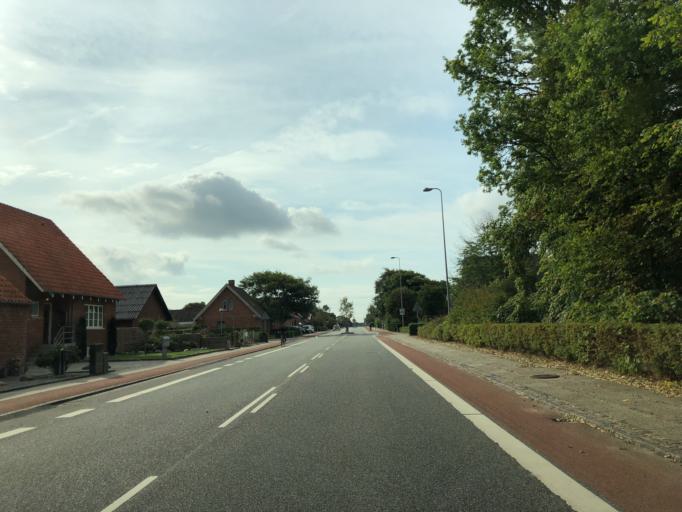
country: DK
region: Central Jutland
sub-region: Ringkobing-Skjern Kommune
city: Skjern
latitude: 55.9396
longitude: 8.5019
